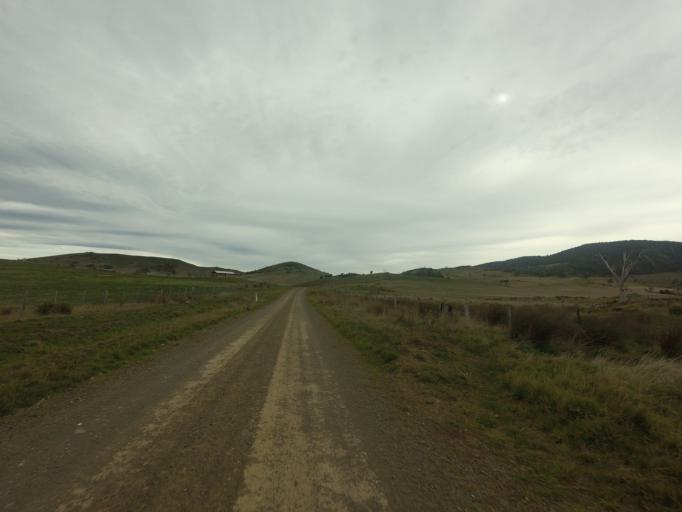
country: AU
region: Tasmania
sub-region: Derwent Valley
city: New Norfolk
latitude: -42.3881
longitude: 146.8795
